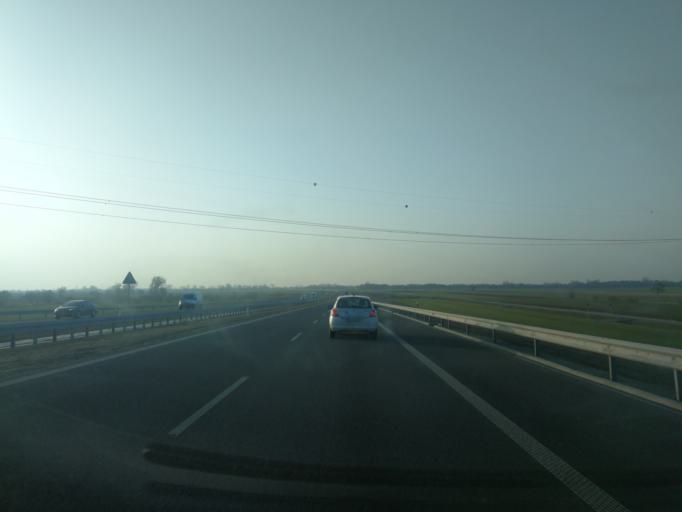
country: PL
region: Warmian-Masurian Voivodeship
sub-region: Powiat elblaski
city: Gronowo Elblaskie
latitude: 54.1673
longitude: 19.2347
